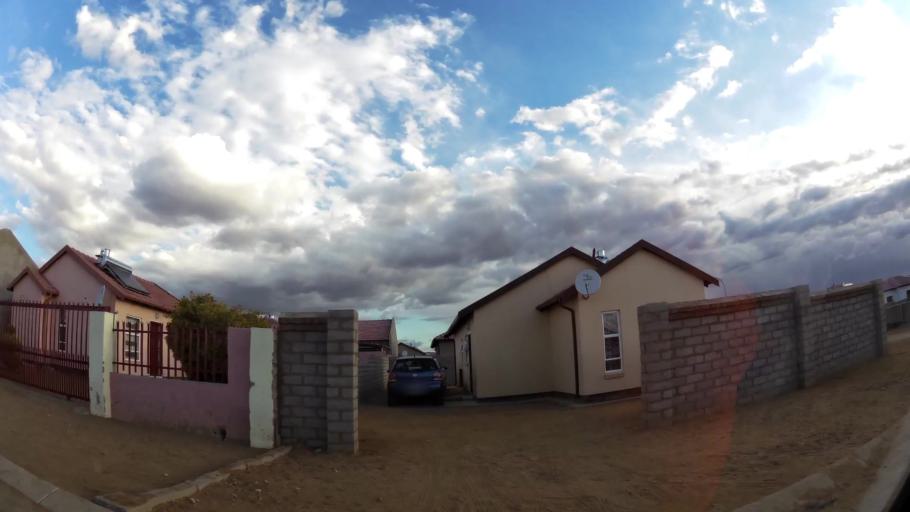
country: ZA
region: Limpopo
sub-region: Capricorn District Municipality
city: Polokwane
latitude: -23.9279
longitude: 29.4157
